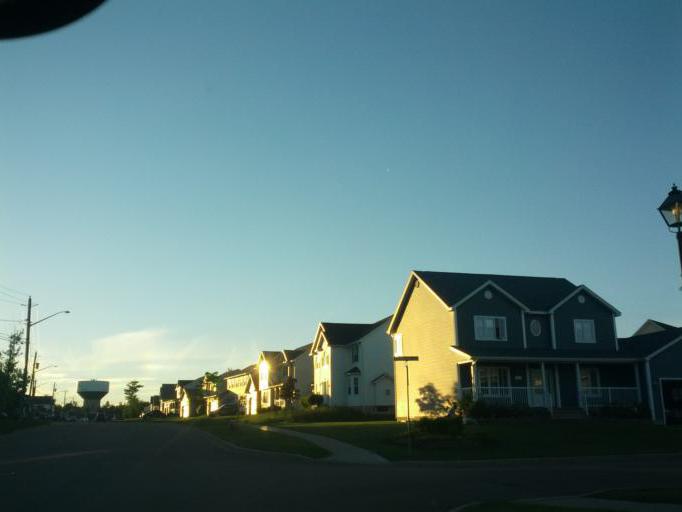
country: CA
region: New Brunswick
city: Moncton
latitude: 46.1116
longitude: -64.8638
